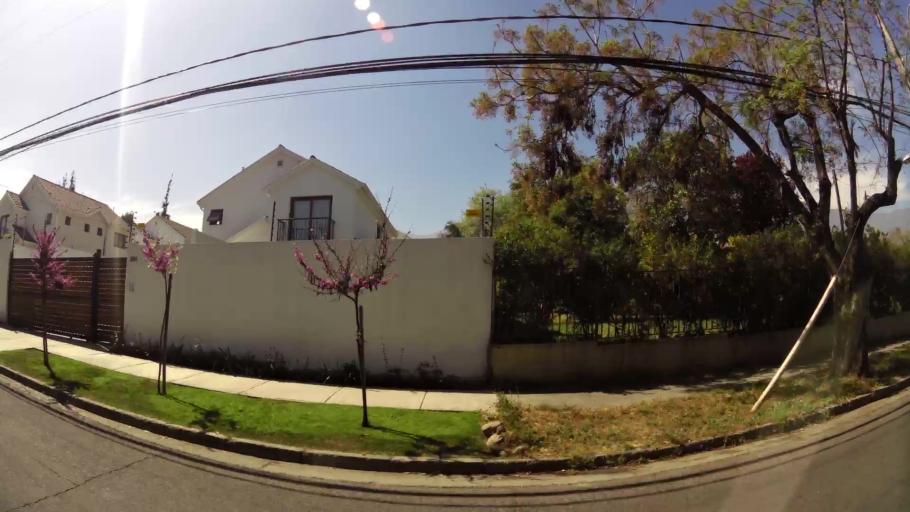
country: CL
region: Santiago Metropolitan
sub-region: Provincia de Santiago
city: Villa Presidente Frei, Nunoa, Santiago, Chile
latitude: -33.4371
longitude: -70.5298
